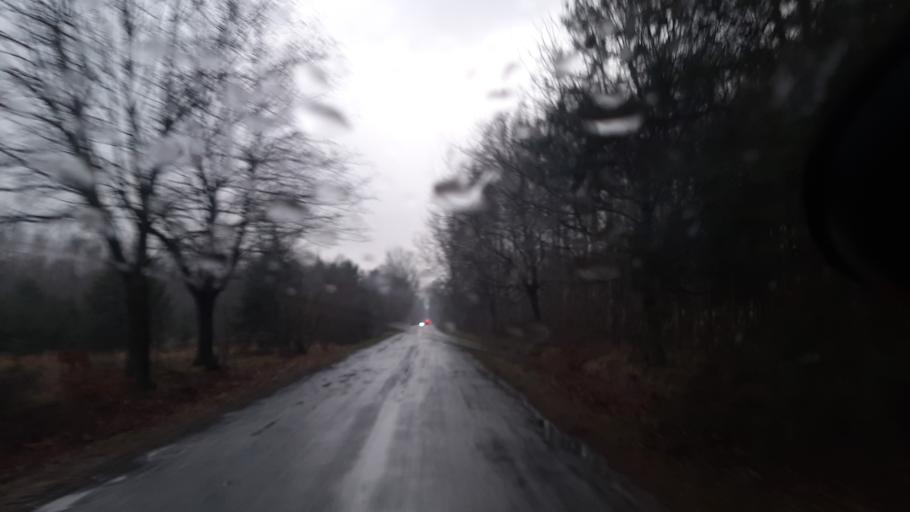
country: PL
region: Lublin Voivodeship
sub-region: Powiat lubartowski
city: Firlej
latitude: 51.5223
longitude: 22.4987
